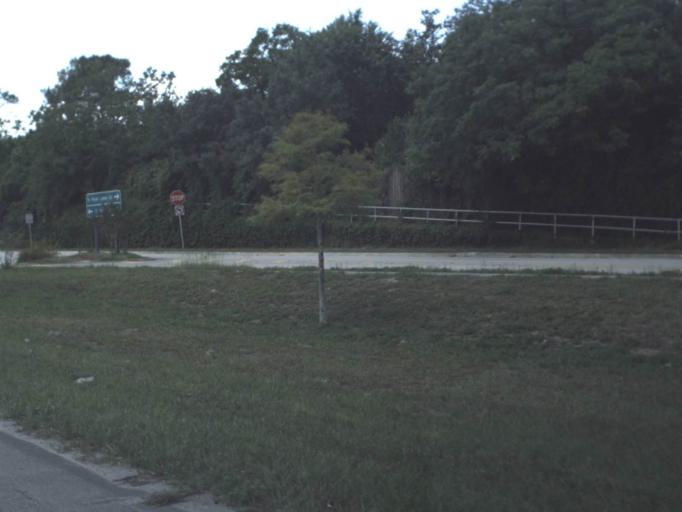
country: US
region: Florida
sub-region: Saint Johns County
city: Fruit Cove
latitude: 30.2147
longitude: -81.5520
